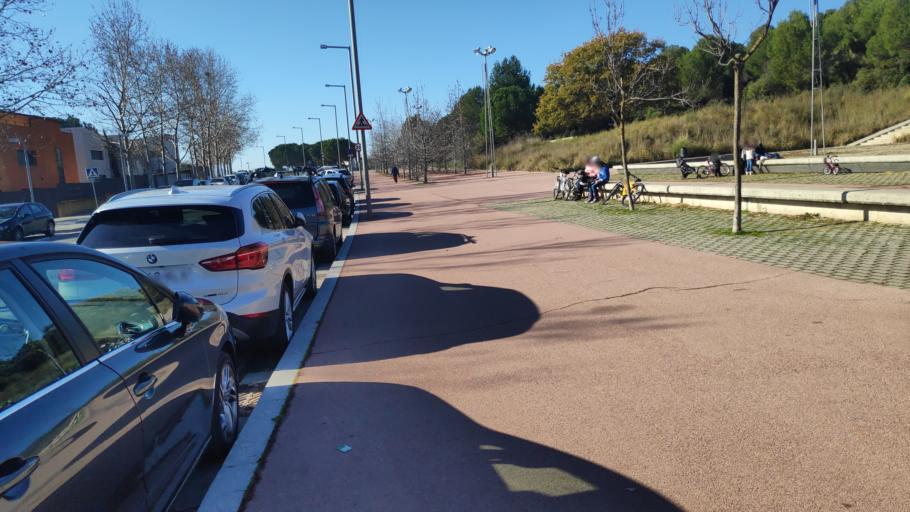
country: ES
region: Catalonia
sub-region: Provincia de Barcelona
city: Sant Cugat del Valles
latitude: 41.4740
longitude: 2.0637
